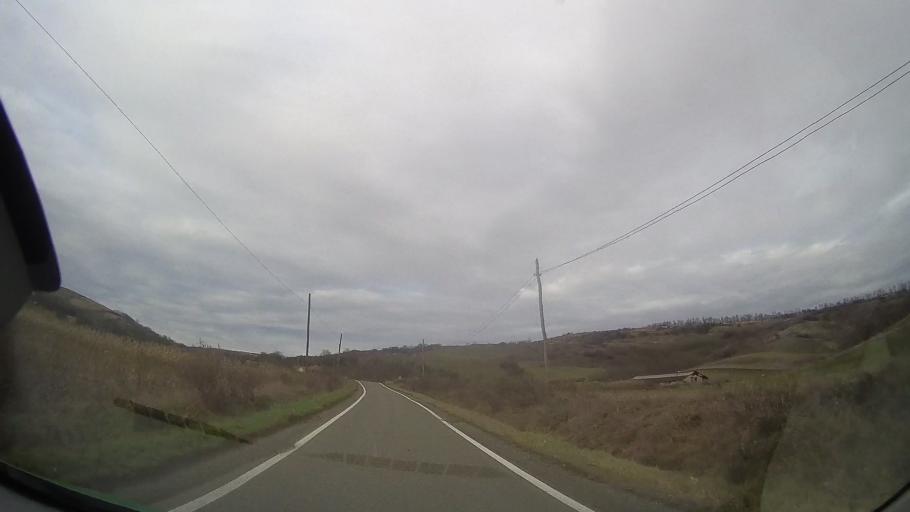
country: RO
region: Mures
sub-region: Comuna Cozma
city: Cozma
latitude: 46.8018
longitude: 24.5348
